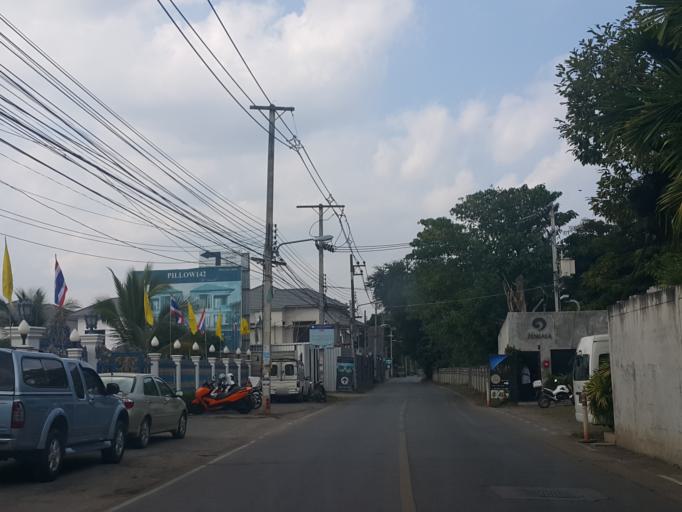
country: TH
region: Chiang Mai
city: Chiang Mai
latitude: 18.8179
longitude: 98.9982
